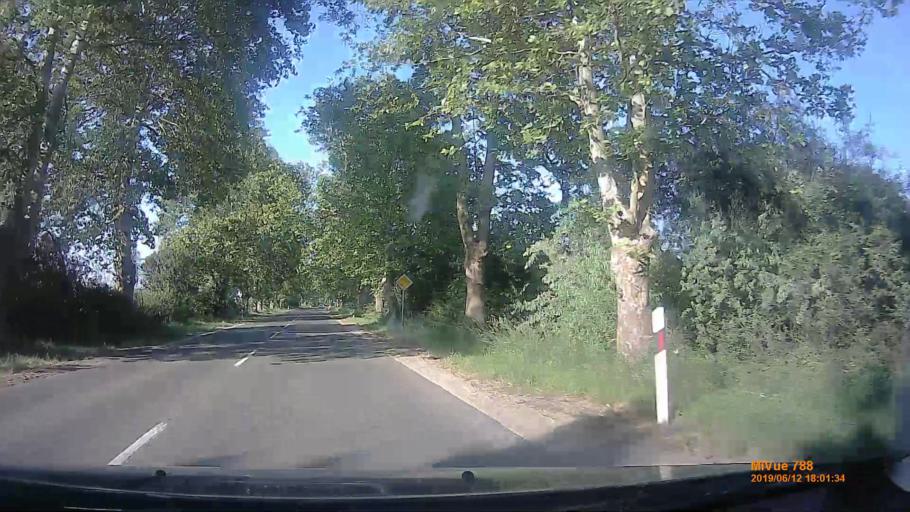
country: HU
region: Csongrad
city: Roszke
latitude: 46.2282
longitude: 20.0763
